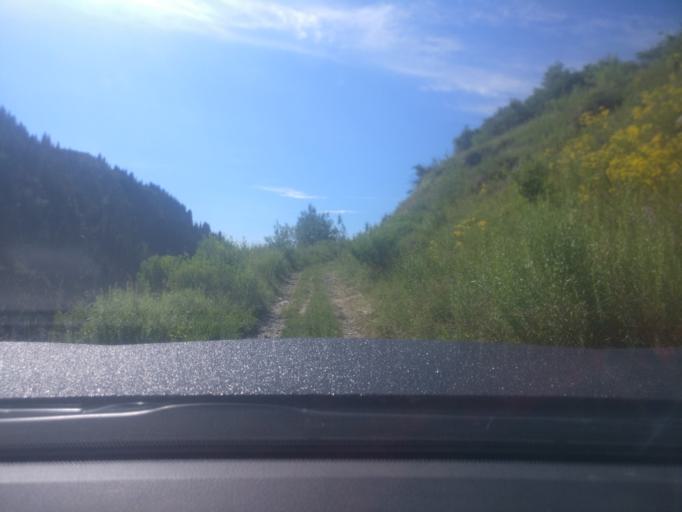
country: KZ
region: Almaty Qalasy
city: Almaty
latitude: 43.0961
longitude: 76.9544
